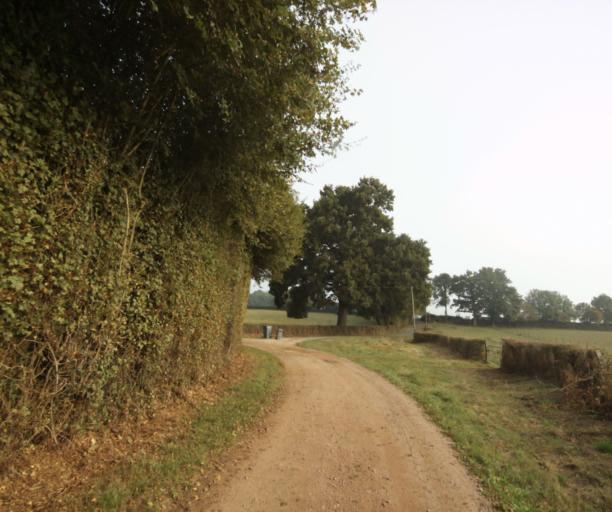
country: FR
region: Bourgogne
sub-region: Departement de Saone-et-Loire
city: Charolles
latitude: 46.4544
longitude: 4.2895
